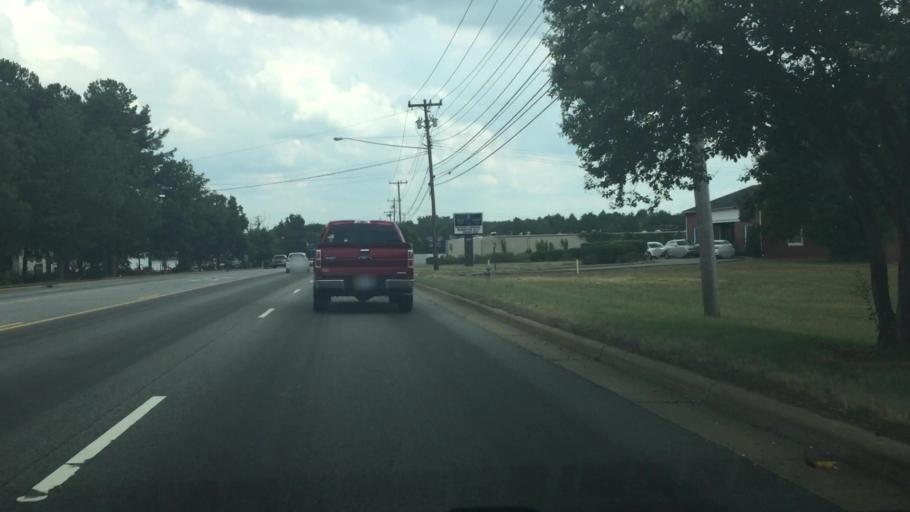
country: US
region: North Carolina
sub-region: Rowan County
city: Salisbury
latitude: 35.6802
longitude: -80.5060
